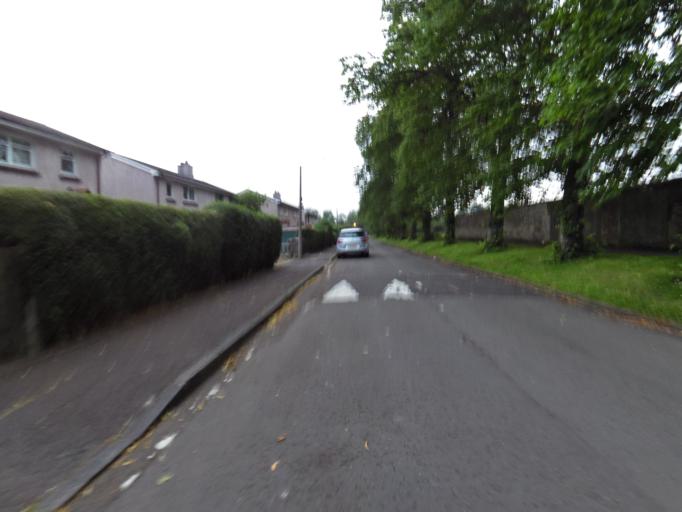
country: GB
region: Scotland
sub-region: Midlothian
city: Loanhead
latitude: 55.9141
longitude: -3.1316
